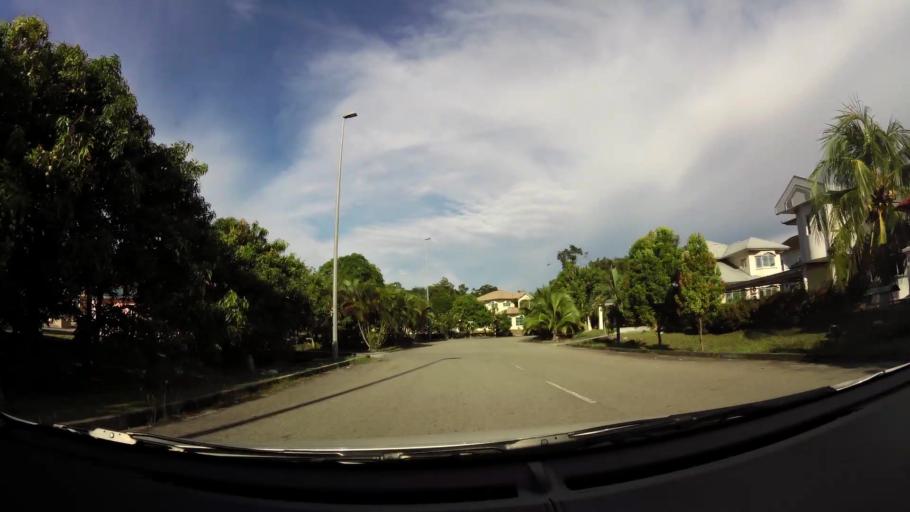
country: BN
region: Brunei and Muara
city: Bandar Seri Begawan
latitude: 4.9844
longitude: 114.9617
